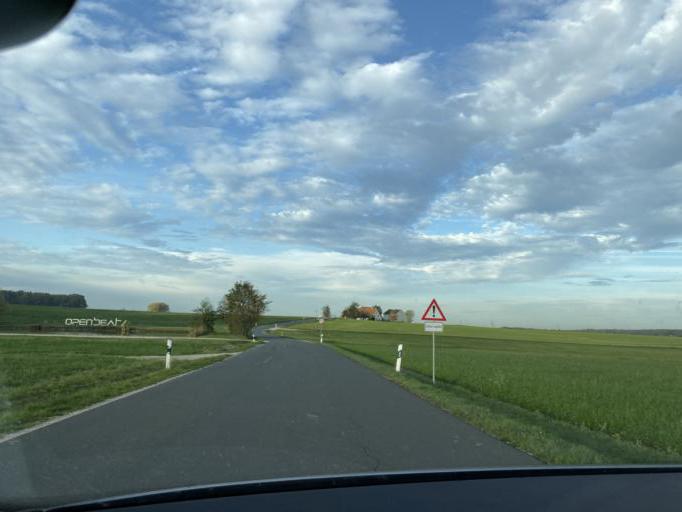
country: DE
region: Bavaria
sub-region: Regierungsbezirk Mittelfranken
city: Puschendorf
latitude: 49.5359
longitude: 10.8336
